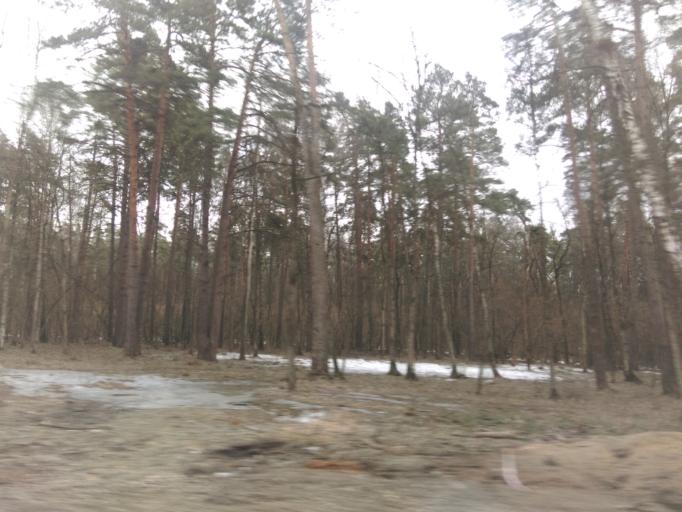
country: RU
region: Moscow
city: Rublevo
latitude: 55.7522
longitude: 37.3345
